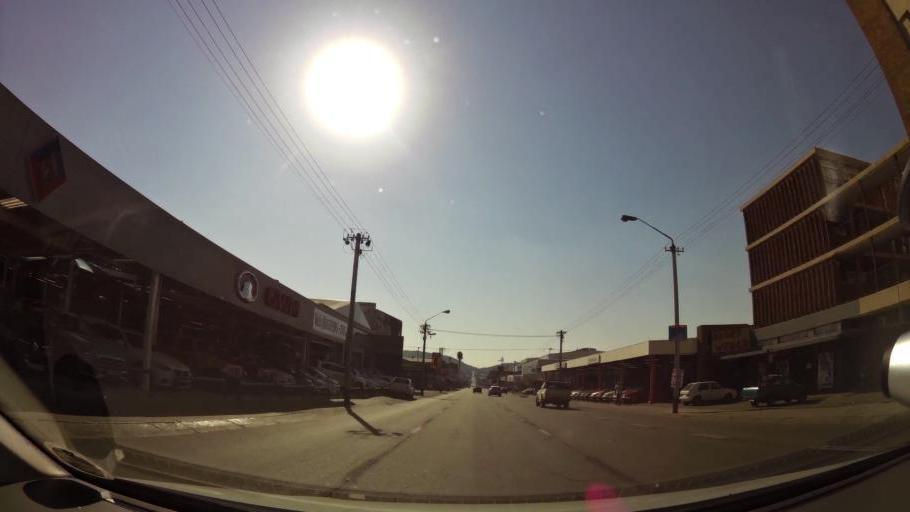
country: ZA
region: Gauteng
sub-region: City of Tshwane Metropolitan Municipality
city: Pretoria
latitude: -25.7173
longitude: 28.2023
